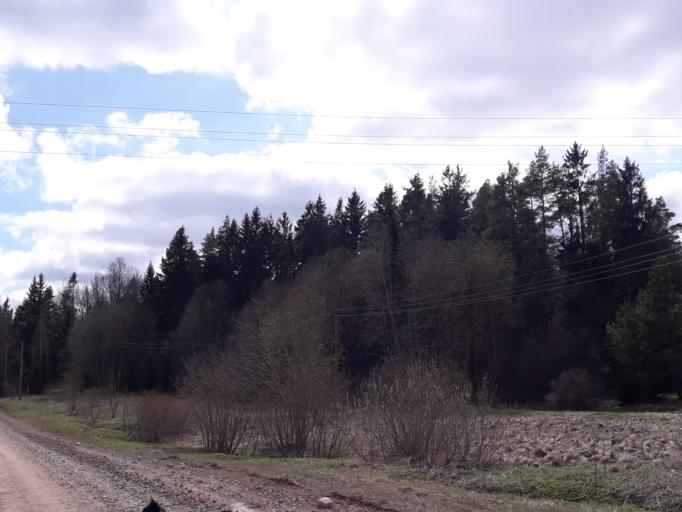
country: LV
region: Talsu Rajons
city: Sabile
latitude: 56.9081
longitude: 22.3995
